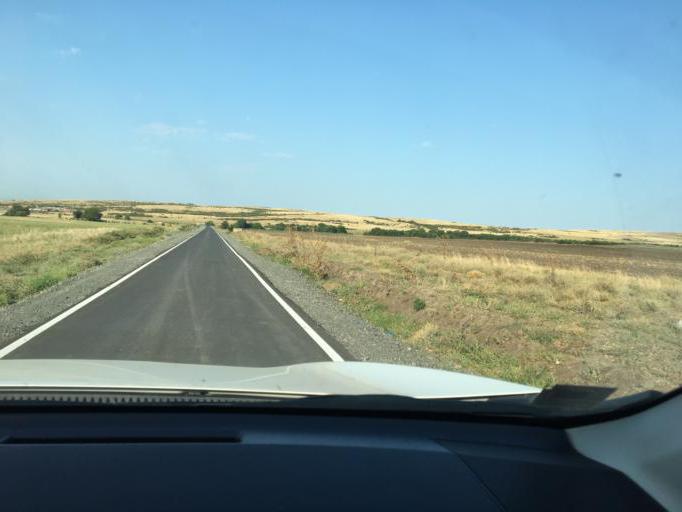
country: BG
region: Burgas
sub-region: Obshtina Burgas
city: Burgas
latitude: 42.6111
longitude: 27.4803
